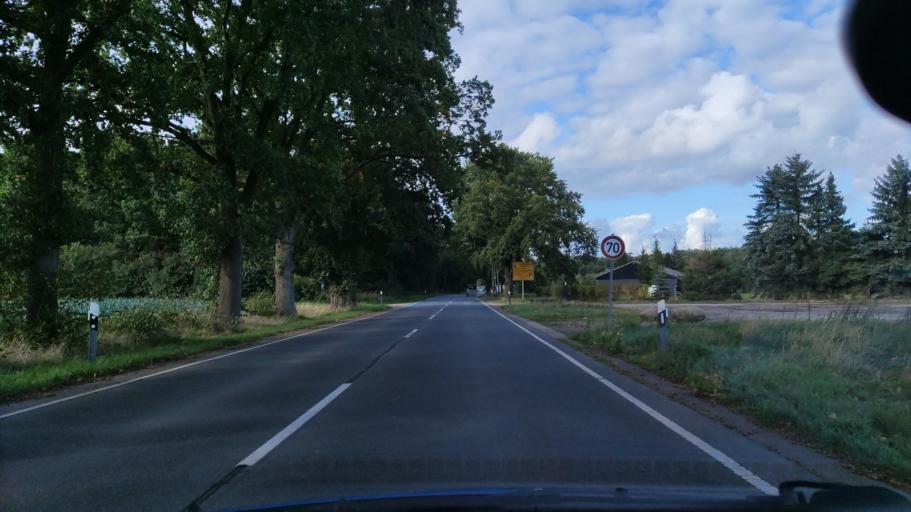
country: DE
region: Lower Saxony
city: Deutsch Evern
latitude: 53.2107
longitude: 10.4447
